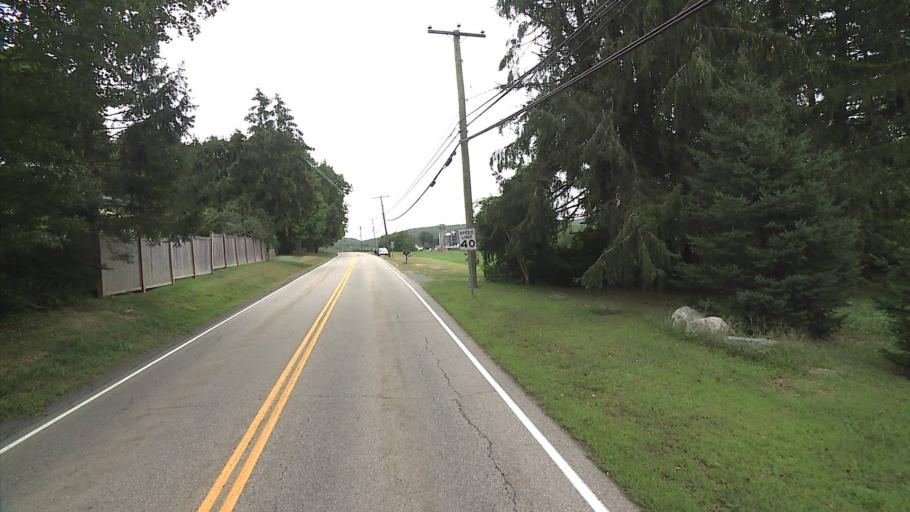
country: US
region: Connecticut
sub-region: Middlesex County
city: Essex Village
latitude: 41.3731
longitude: -72.3473
